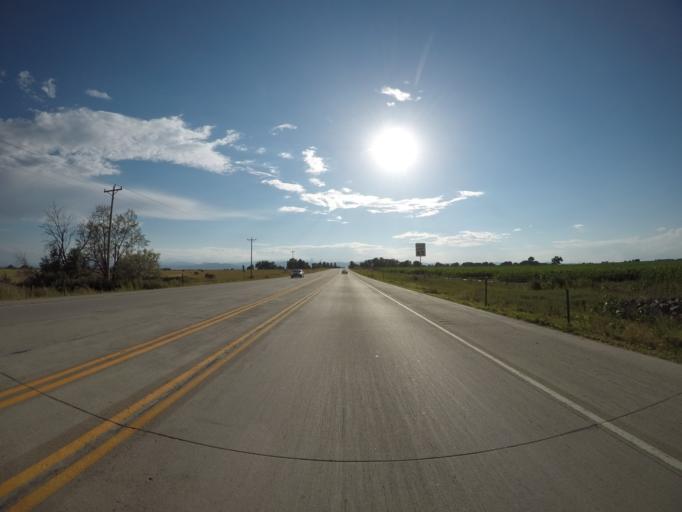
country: US
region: Colorado
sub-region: Weld County
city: Severance
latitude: 40.5809
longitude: -104.9451
